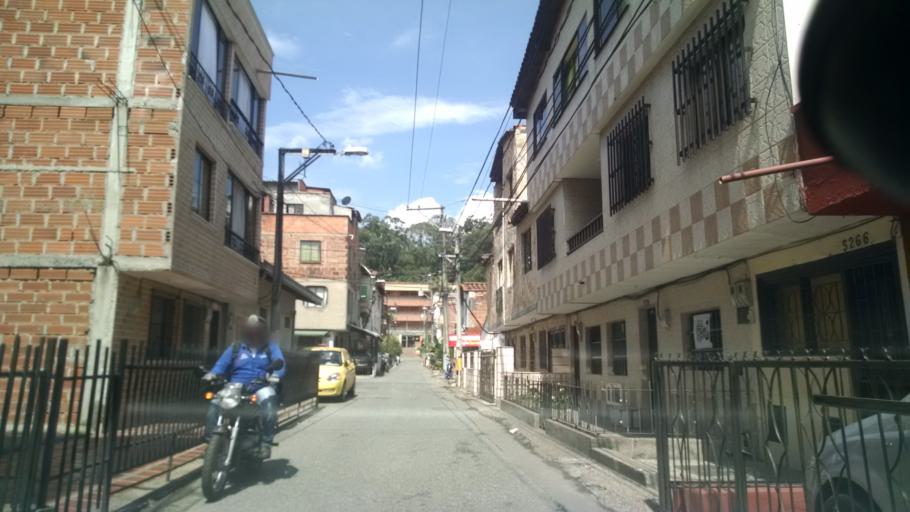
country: CO
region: Antioquia
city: Itagui
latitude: 6.2018
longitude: -75.5887
